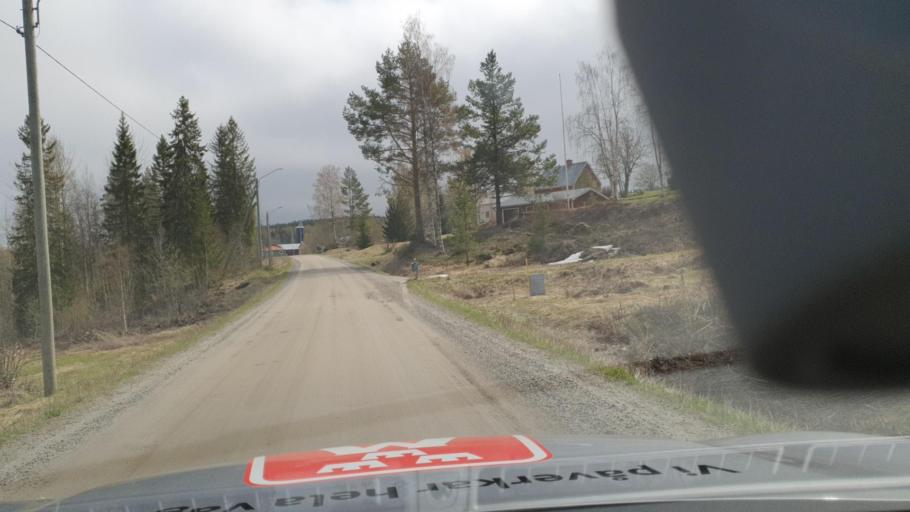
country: SE
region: Vaesterbotten
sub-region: Bjurholms Kommun
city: Bjurholm
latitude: 63.6715
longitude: 18.9992
